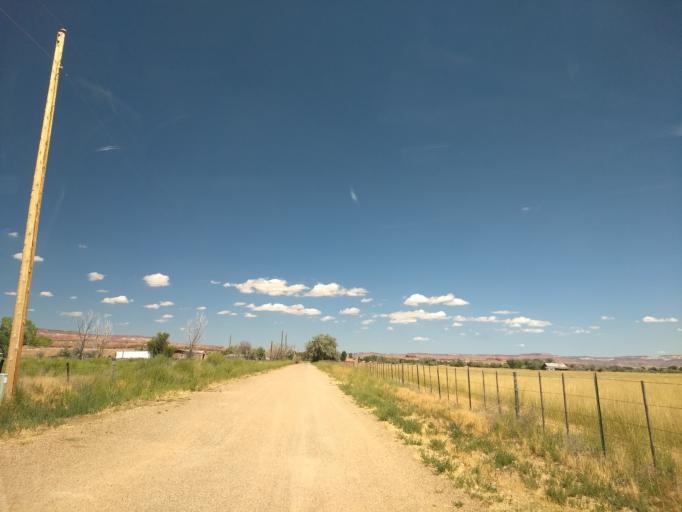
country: US
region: Arizona
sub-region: Coconino County
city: Fredonia
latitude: 36.9300
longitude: -112.5353
